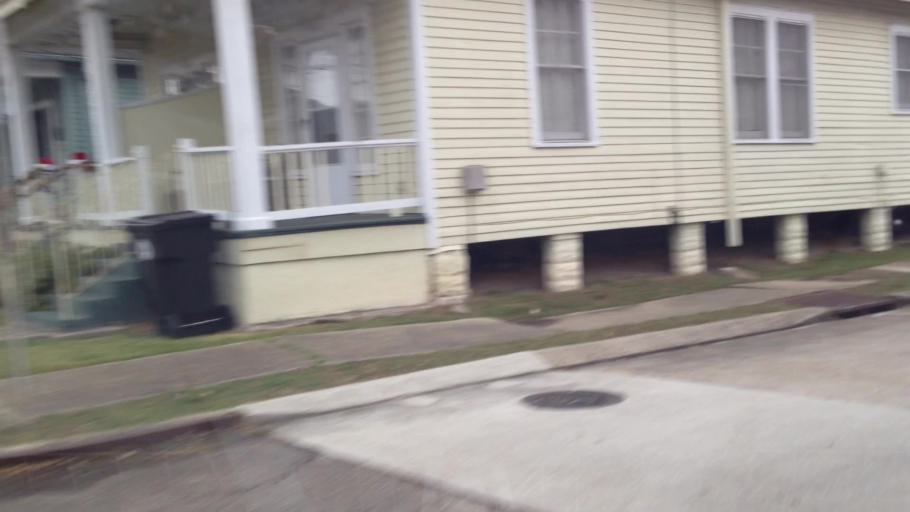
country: US
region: Louisiana
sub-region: Orleans Parish
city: New Orleans
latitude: 29.9518
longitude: -90.1056
